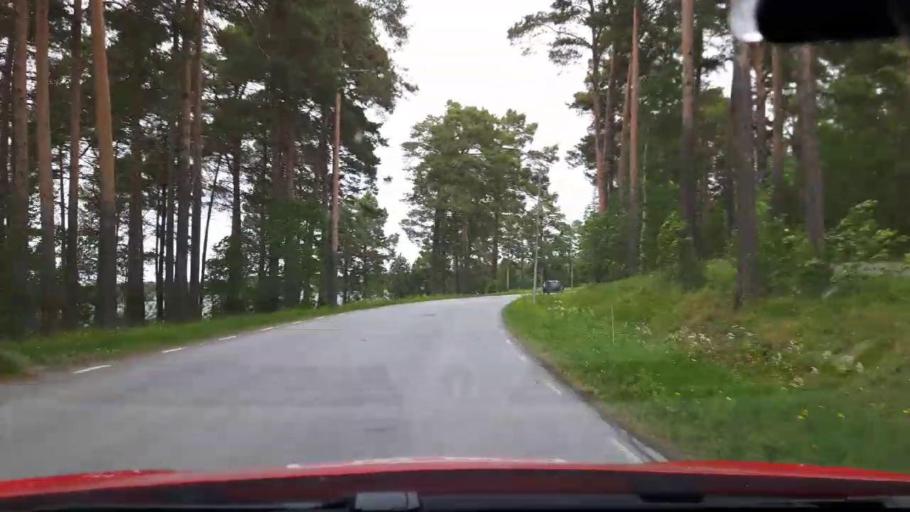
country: SE
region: Jaemtland
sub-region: OEstersunds Kommun
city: Ostersund
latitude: 63.1934
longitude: 14.6323
